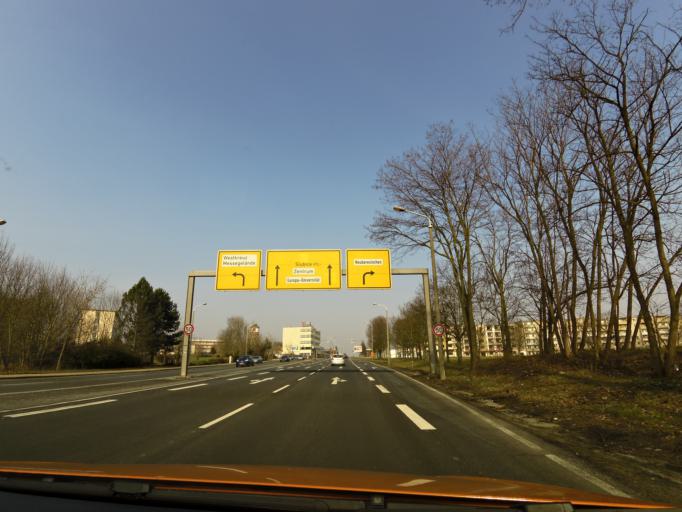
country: DE
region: Brandenburg
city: Frankfurt (Oder)
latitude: 52.3281
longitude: 14.5349
